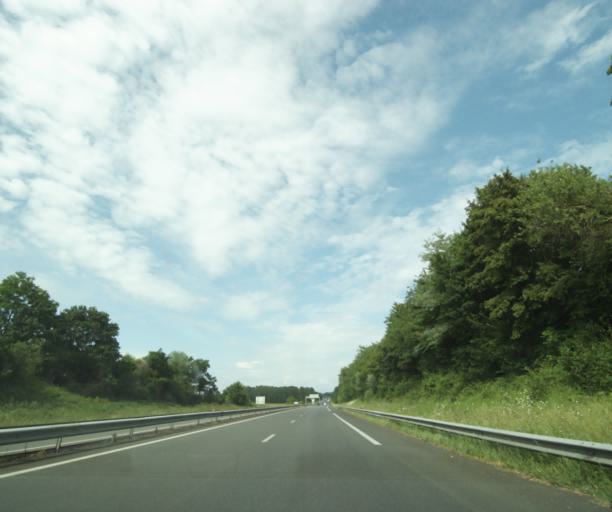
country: FR
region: Pays de la Loire
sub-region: Departement de Maine-et-Loire
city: Seiches-sur-le-Loir
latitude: 47.5858
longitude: -0.3284
